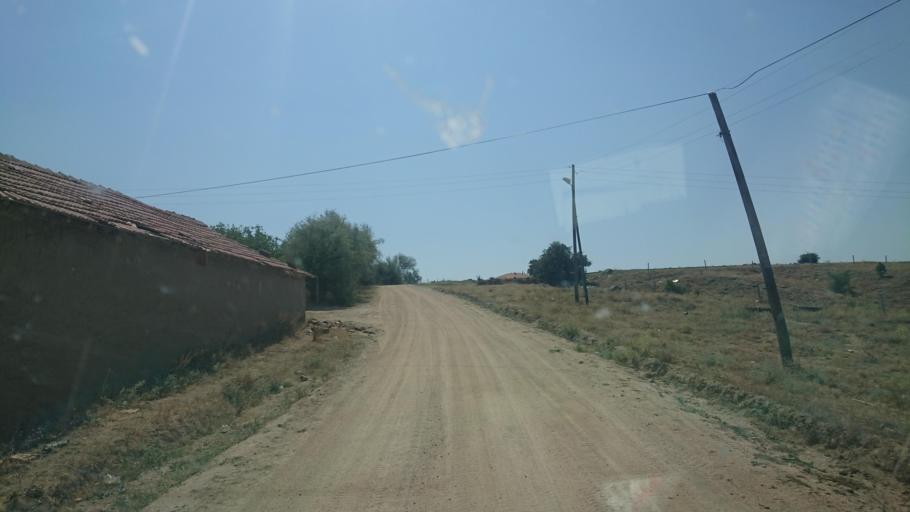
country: TR
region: Aksaray
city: Agacoren
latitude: 38.8165
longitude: 33.9542
